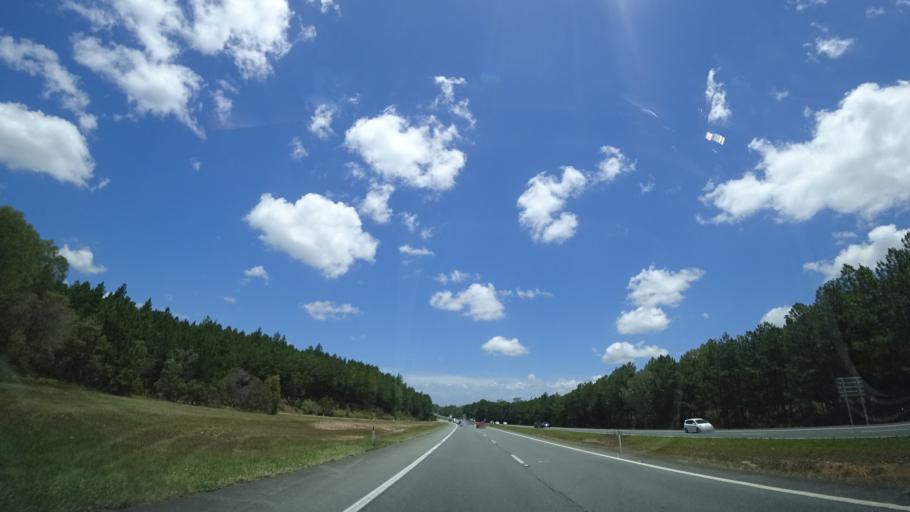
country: AU
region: Queensland
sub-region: Moreton Bay
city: Caboolture
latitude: -26.9892
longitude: 152.9785
